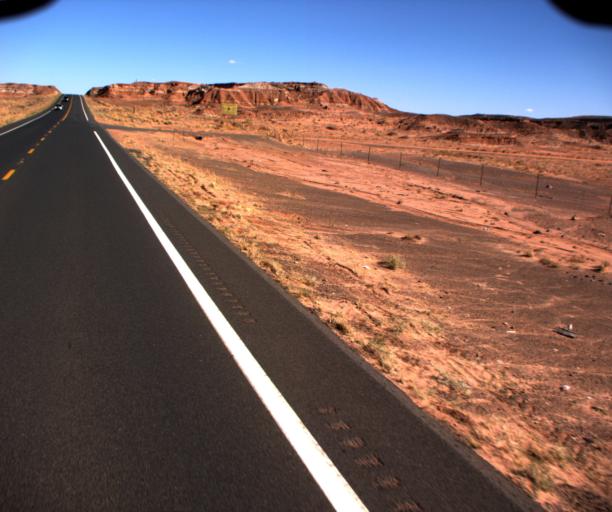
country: US
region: Arizona
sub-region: Coconino County
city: Tuba City
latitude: 36.1021
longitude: -111.2935
